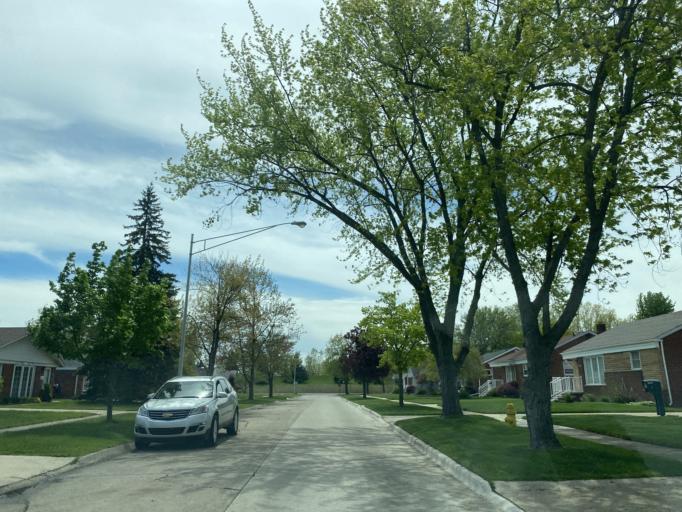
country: US
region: Michigan
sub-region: Wayne County
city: Riverview
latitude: 42.1717
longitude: -83.1861
